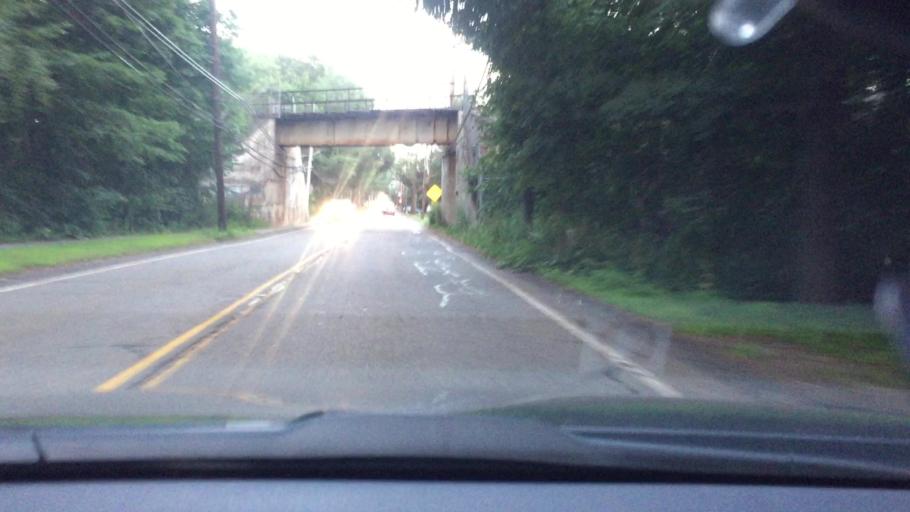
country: US
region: Massachusetts
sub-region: Norfolk County
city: Needham
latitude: 42.2745
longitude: -71.2280
